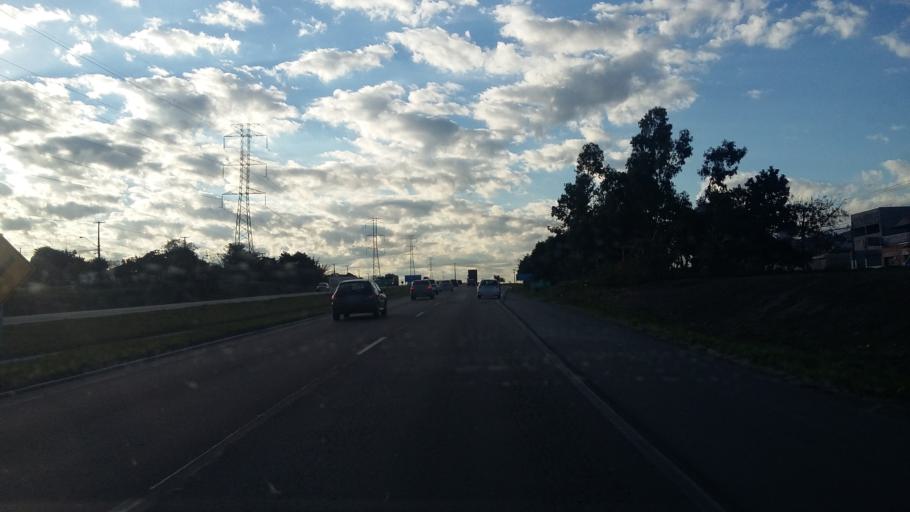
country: BR
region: Parana
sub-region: Curitiba
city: Curitiba
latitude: -25.4895
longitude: -49.3453
